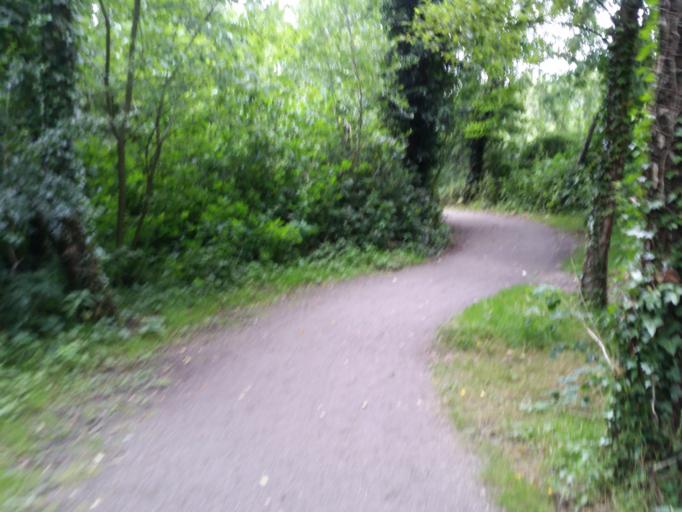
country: GB
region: Northern Ireland
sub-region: Castlereagh District
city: Castlereagh
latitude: 54.6091
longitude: -5.8847
